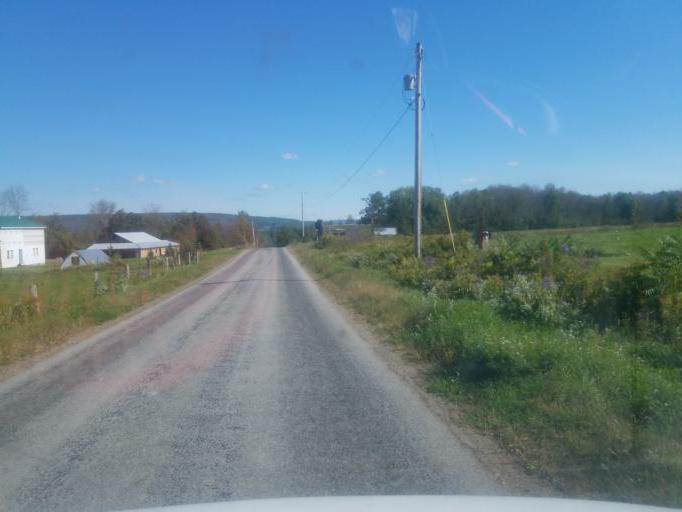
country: US
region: New York
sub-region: Allegany County
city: Friendship
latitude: 42.3149
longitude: -78.1203
